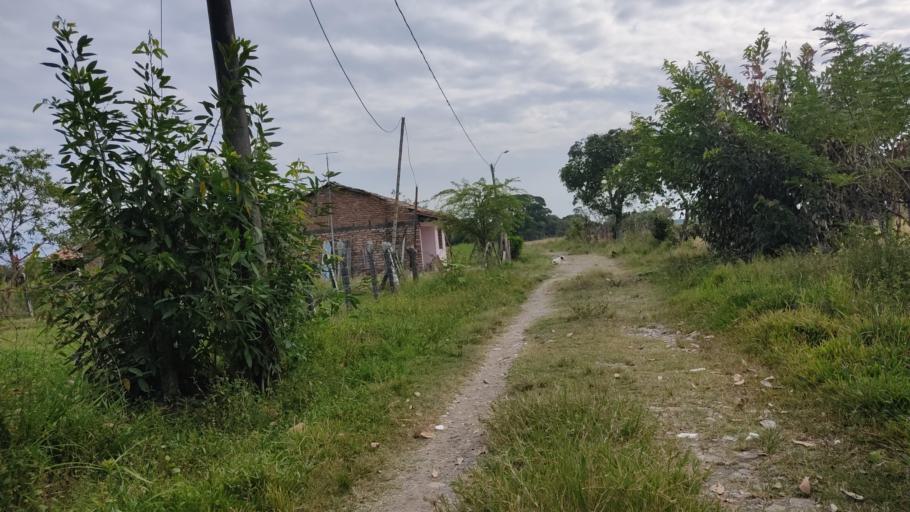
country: CO
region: Valle del Cauca
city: Jamundi
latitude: 3.1323
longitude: -76.5594
